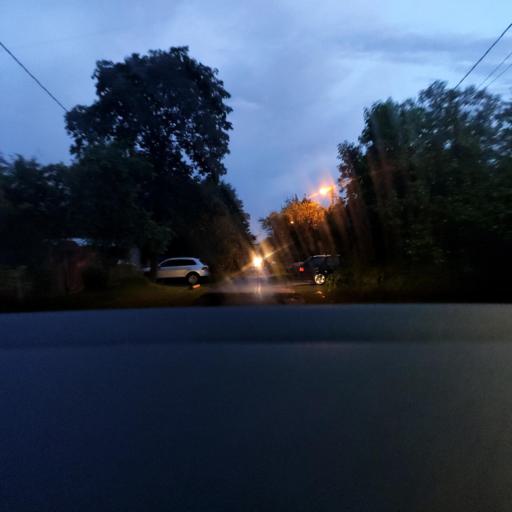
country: RU
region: Moskovskaya
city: Sheremet'yevskiy
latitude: 55.9993
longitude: 37.5457
